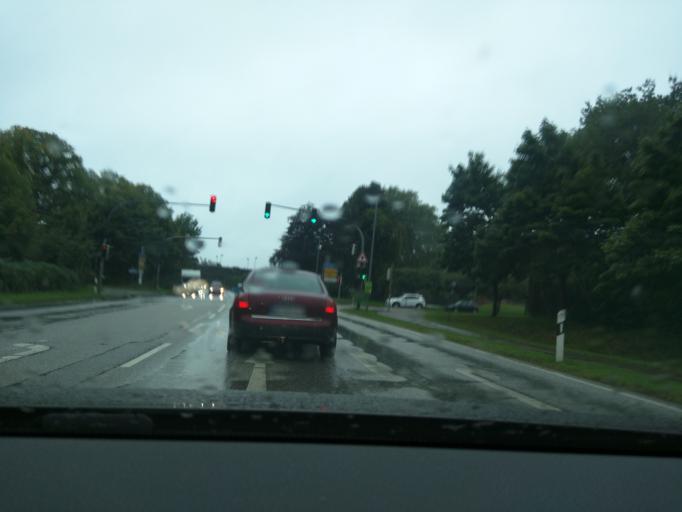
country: DE
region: Schleswig-Holstein
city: Schwarzenbek
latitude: 53.5051
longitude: 10.4813
